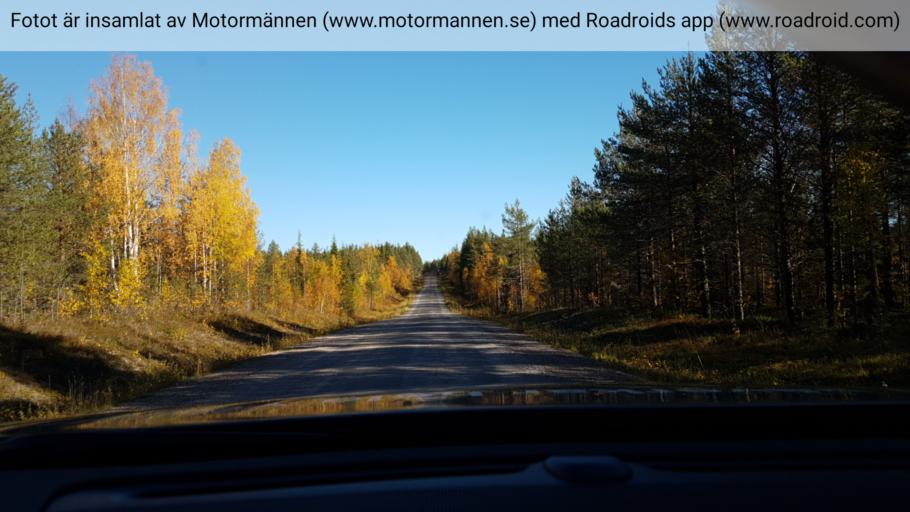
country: SE
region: Norrbotten
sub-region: Gallivare Kommun
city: Gaellivare
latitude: 66.5279
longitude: 20.9626
